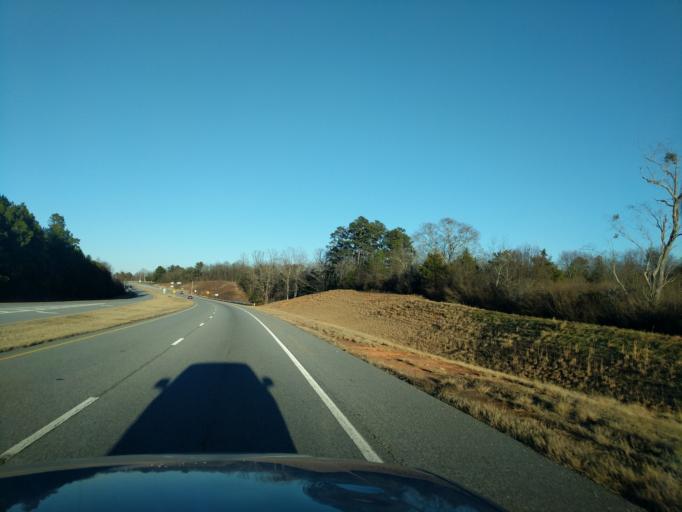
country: US
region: Georgia
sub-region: Stephens County
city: Toccoa
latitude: 34.5445
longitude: -83.2840
